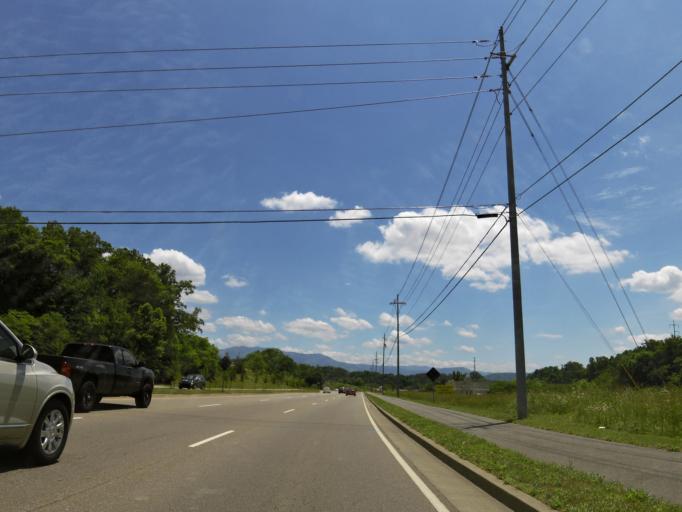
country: US
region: Tennessee
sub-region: Sevier County
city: Pigeon Forge
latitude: 35.8161
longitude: -83.5385
